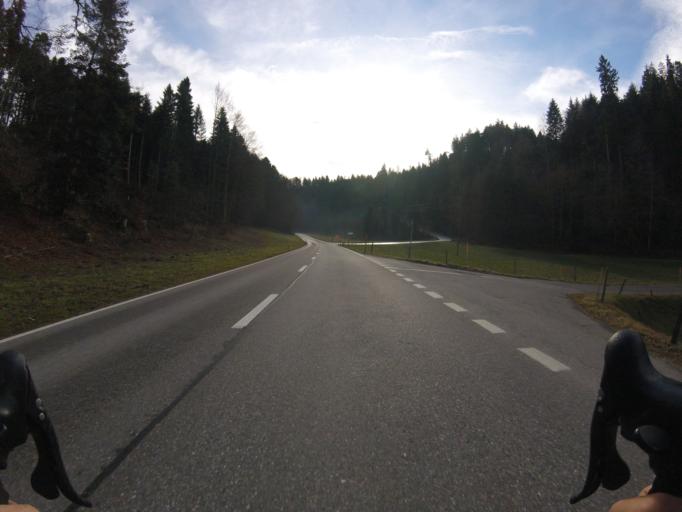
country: CH
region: Fribourg
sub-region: Sense District
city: Ueberstorf
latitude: 46.8467
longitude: 7.3222
